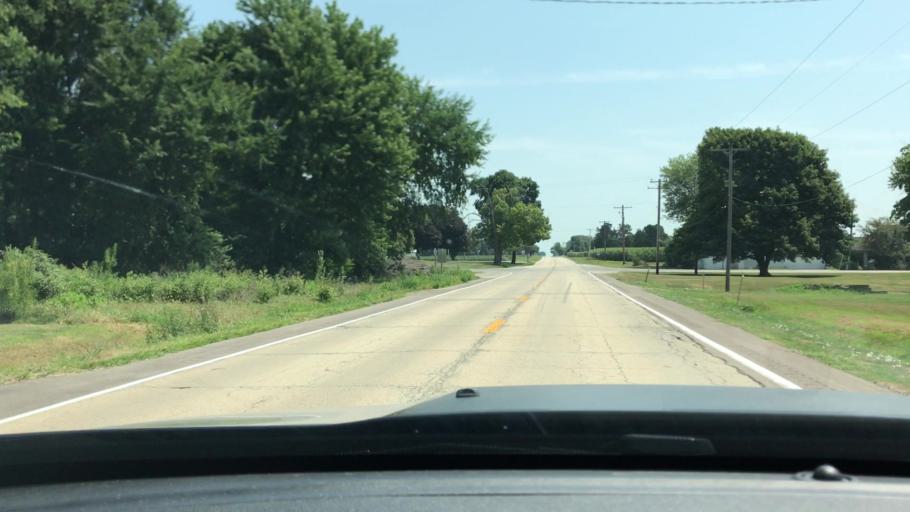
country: US
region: Illinois
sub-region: LaSalle County
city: Earlville
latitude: 41.4689
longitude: -88.9358
